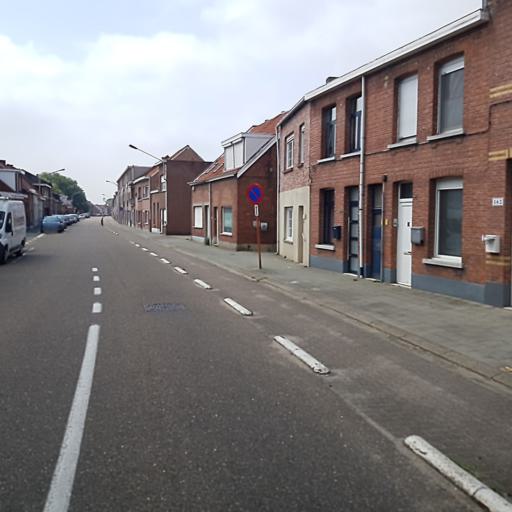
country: BE
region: Flanders
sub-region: Provincie Antwerpen
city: Kapellen
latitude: 51.3108
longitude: 4.4217
